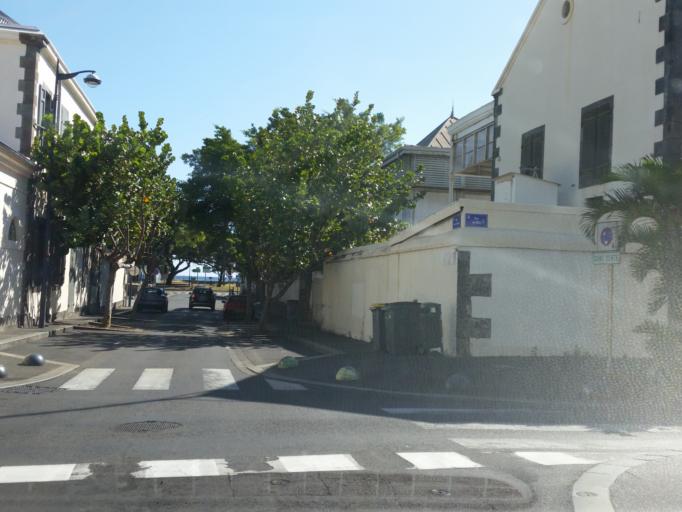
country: RE
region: Reunion
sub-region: Reunion
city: Saint-Denis
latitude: -20.8738
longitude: 55.4486
